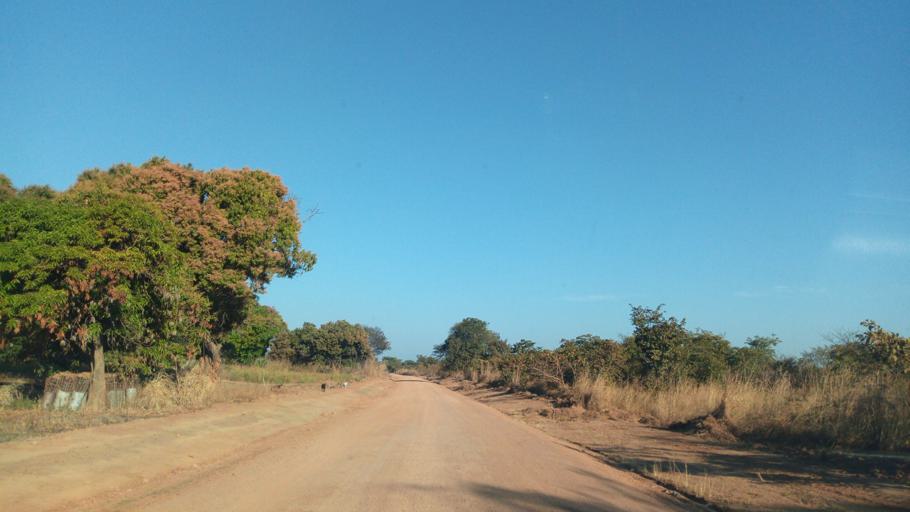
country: ZM
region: Luapula
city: Mwense
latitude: -10.4453
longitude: 28.5727
